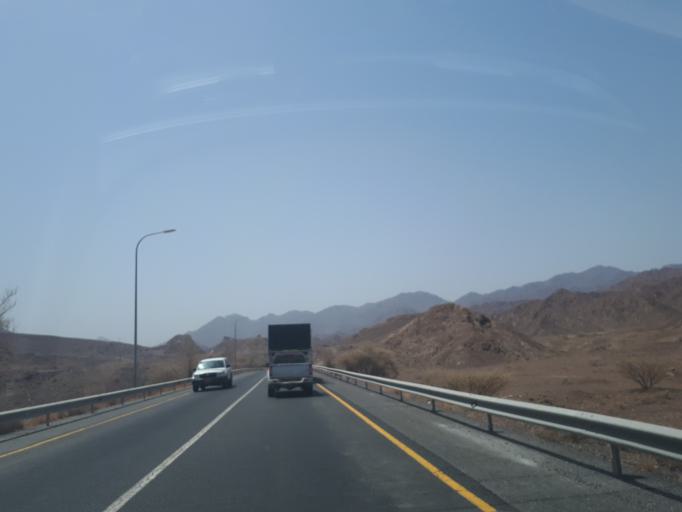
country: OM
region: Muhafazat ad Dakhiliyah
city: Sufalat Sama'il
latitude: 23.2067
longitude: 58.0809
